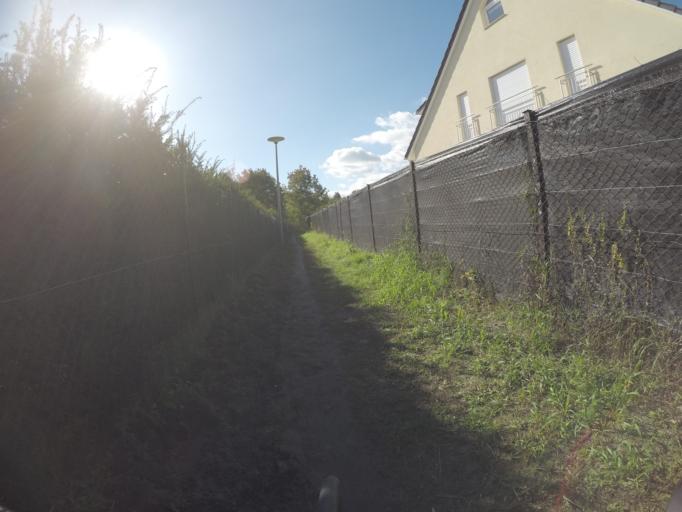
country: DE
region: Berlin
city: Staaken
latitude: 52.5305
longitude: 13.1354
